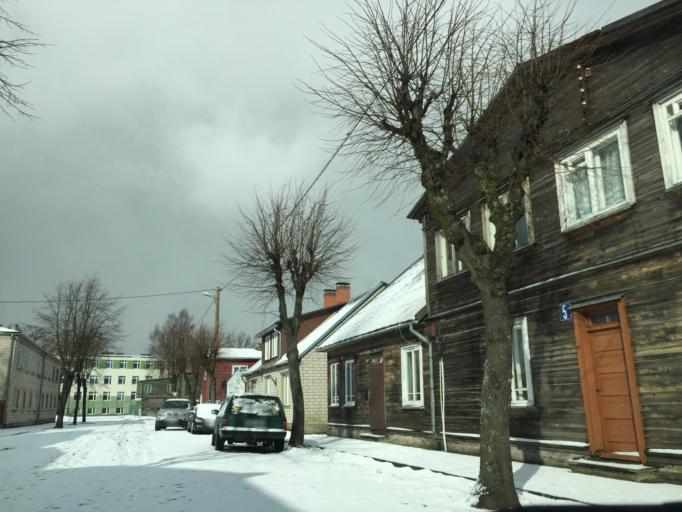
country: LV
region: Ventspils
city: Ventspils
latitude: 57.3929
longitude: 21.5576
